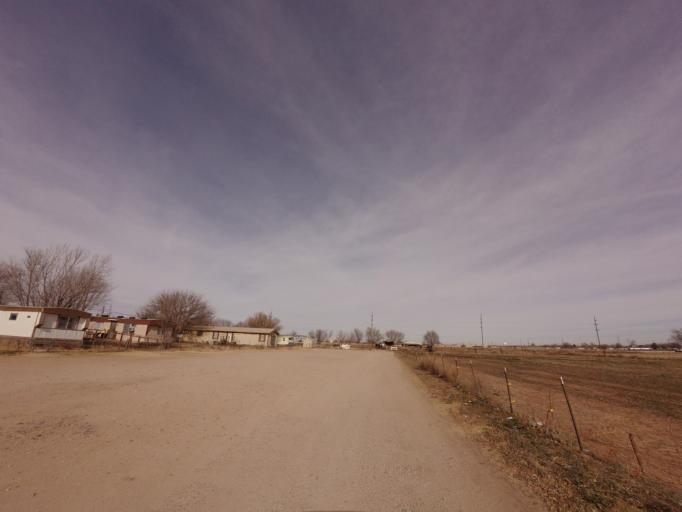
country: US
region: New Mexico
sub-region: Curry County
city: Clovis
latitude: 34.4108
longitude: -103.2342
